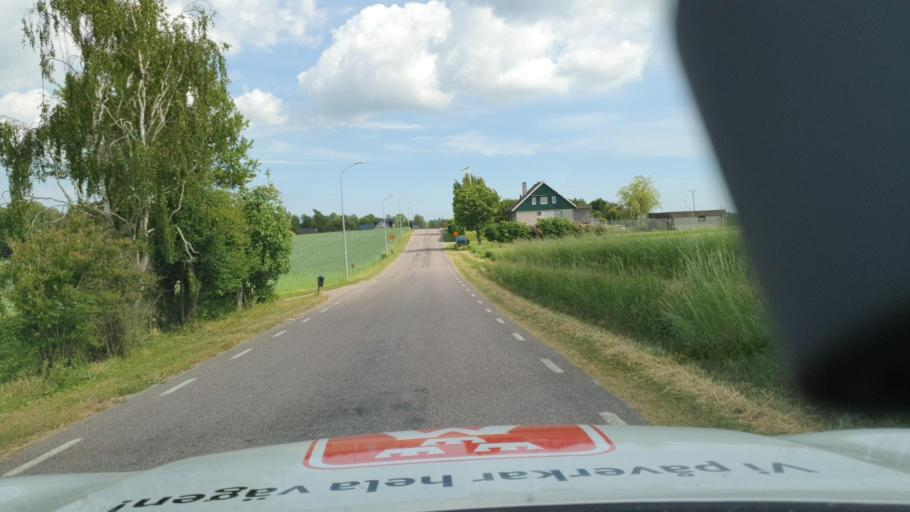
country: SE
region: Skane
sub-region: Skurups Kommun
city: Skurup
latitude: 55.5121
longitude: 13.5417
